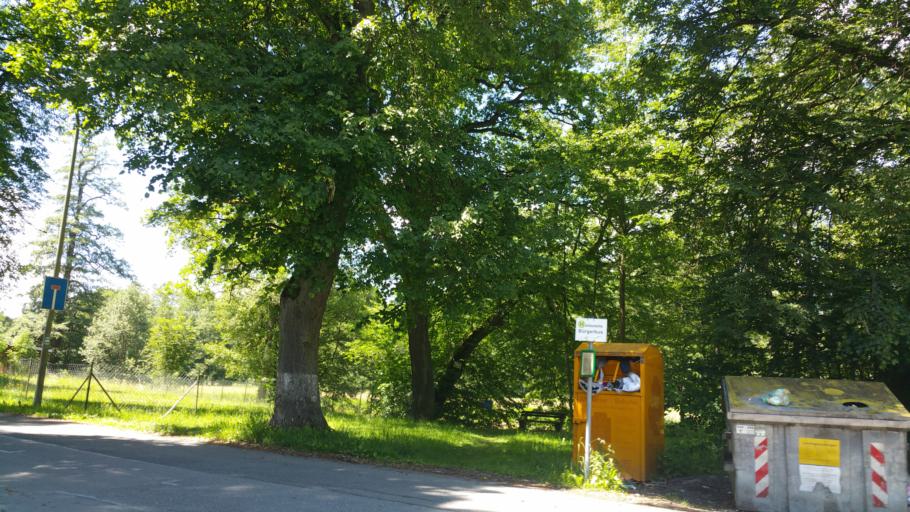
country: DE
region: Bavaria
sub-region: Upper Franconia
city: Schwarzenbach an der Saale
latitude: 50.2176
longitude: 11.9324
